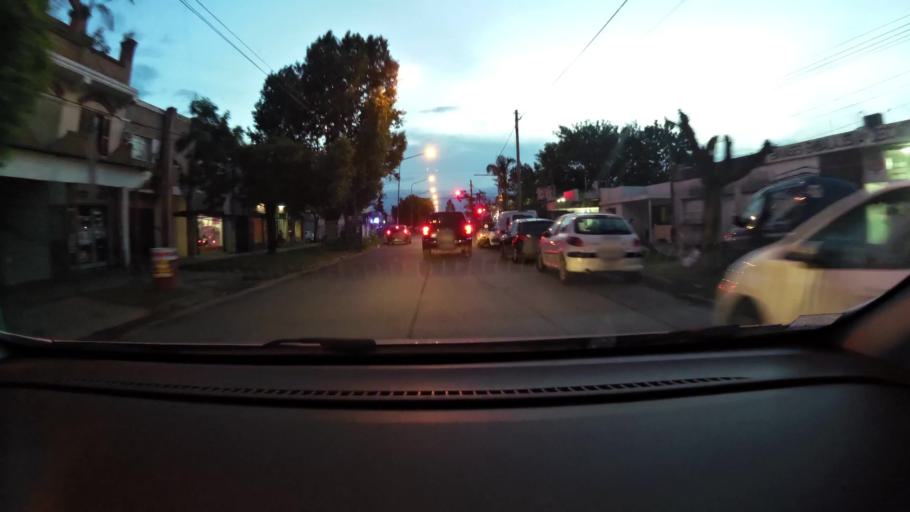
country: AR
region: Buenos Aires
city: San Nicolas de los Arroyos
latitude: -33.3448
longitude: -60.2307
